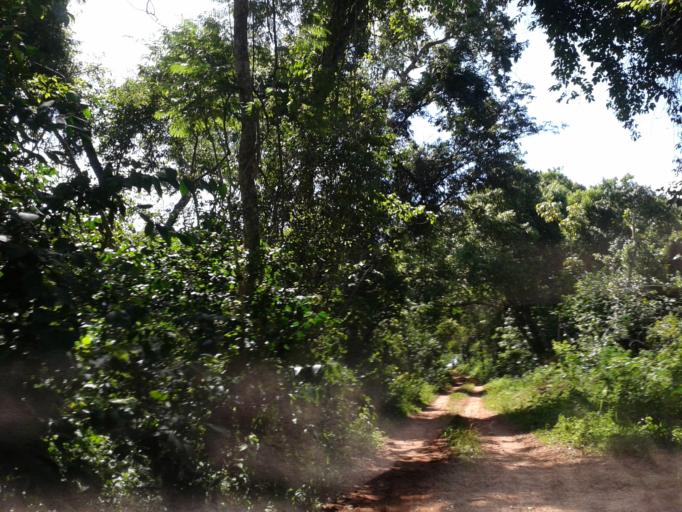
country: BR
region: Minas Gerais
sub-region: Santa Vitoria
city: Santa Vitoria
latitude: -19.1417
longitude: -50.5482
